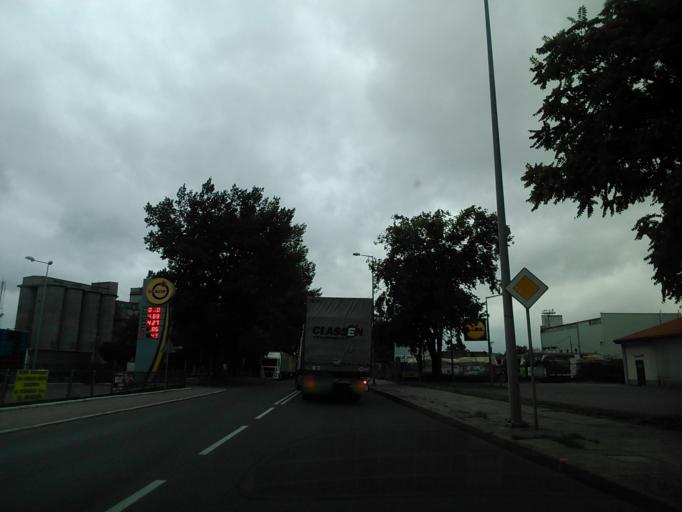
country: PL
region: Kujawsko-Pomorskie
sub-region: Powiat inowroclawski
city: Kruszwica
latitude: 52.6785
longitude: 18.3146
